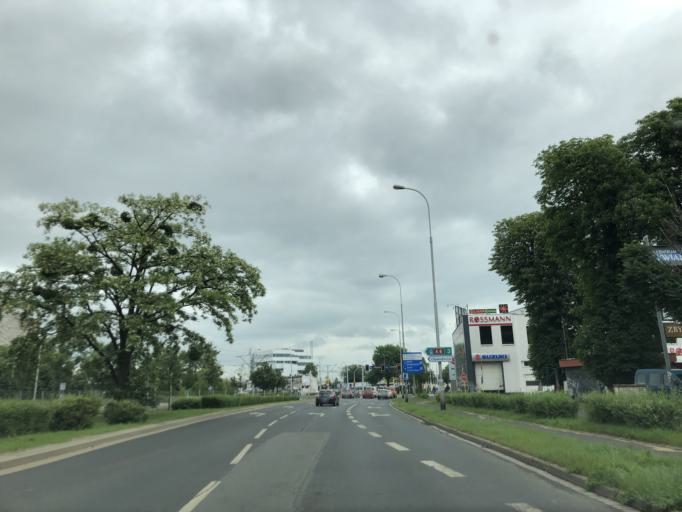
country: PL
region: Lower Silesian Voivodeship
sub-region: Powiat wroclawski
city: Wroclaw
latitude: 51.1387
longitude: 17.0313
